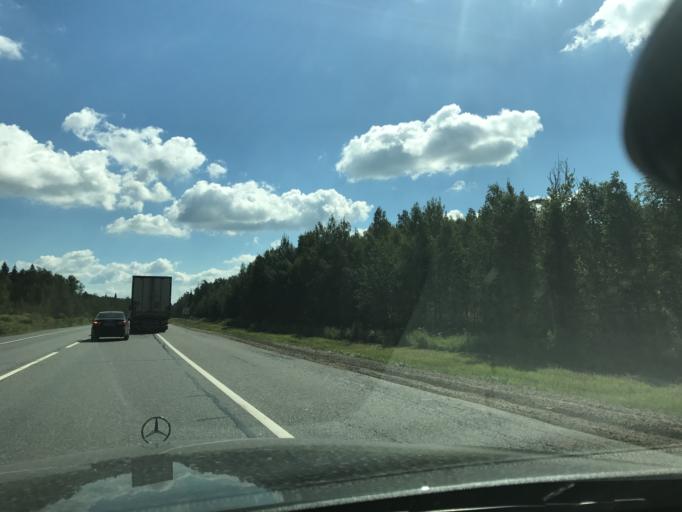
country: RU
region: Vladimir
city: Raduzhnyy
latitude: 56.0713
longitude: 40.2842
